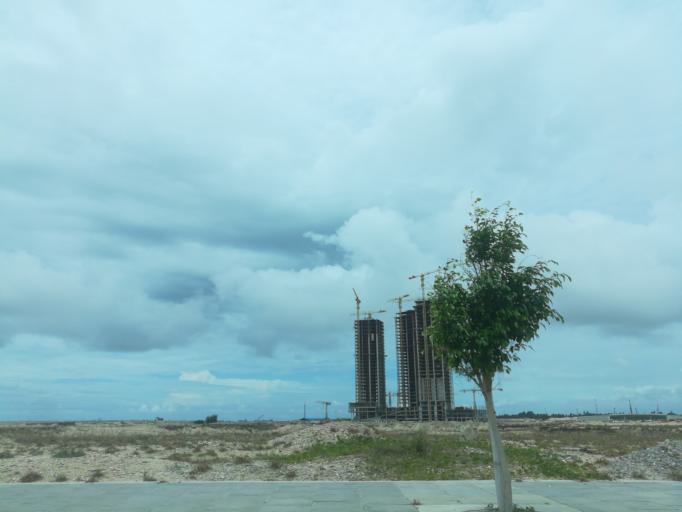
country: NG
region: Lagos
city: Lagos
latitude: 6.4041
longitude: 3.4123
